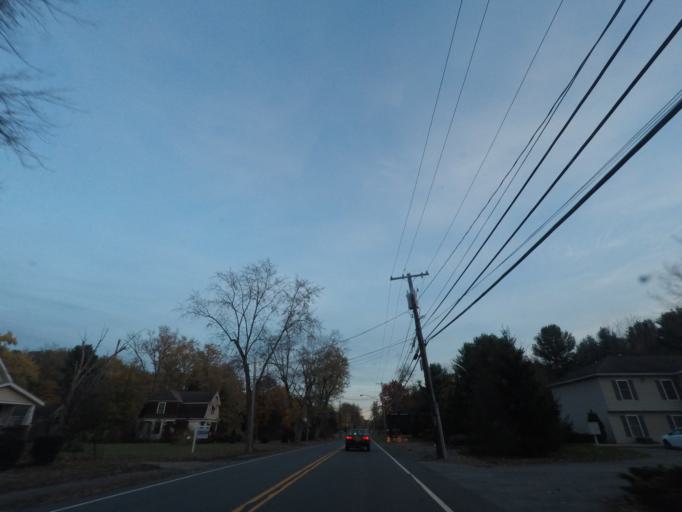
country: US
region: New York
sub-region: Schenectady County
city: Rotterdam
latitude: 42.7703
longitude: -73.9462
